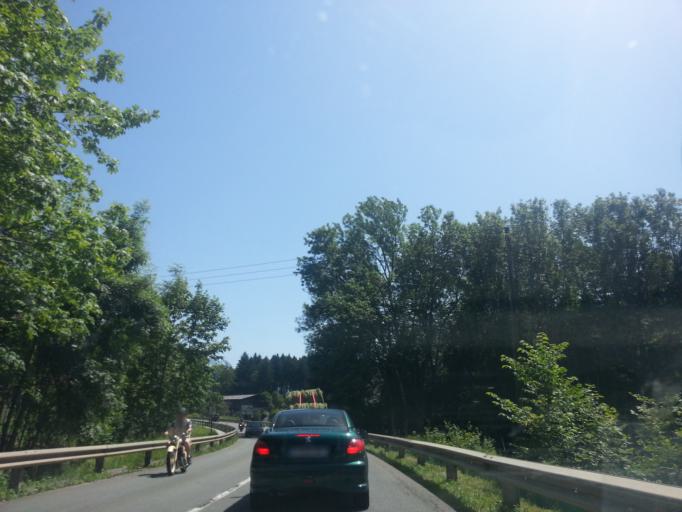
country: AT
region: Salzburg
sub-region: Politischer Bezirk Hallein
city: Adnet
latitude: 47.6665
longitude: 13.1221
